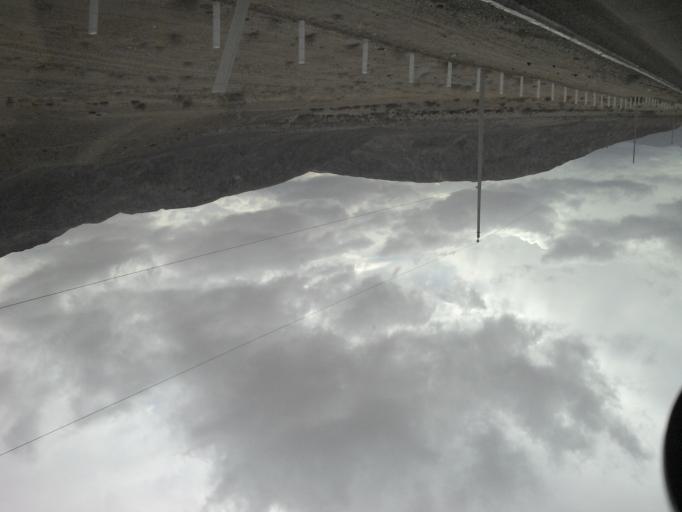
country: MX
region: Baja California
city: Progreso
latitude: 32.5897
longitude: -115.6990
